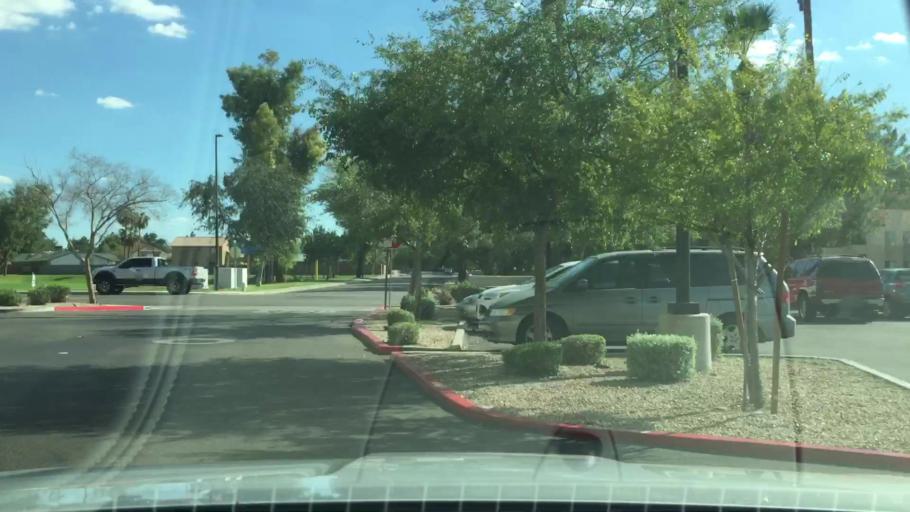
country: US
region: Arizona
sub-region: Maricopa County
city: Gilbert
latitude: 33.3721
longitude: -111.7884
